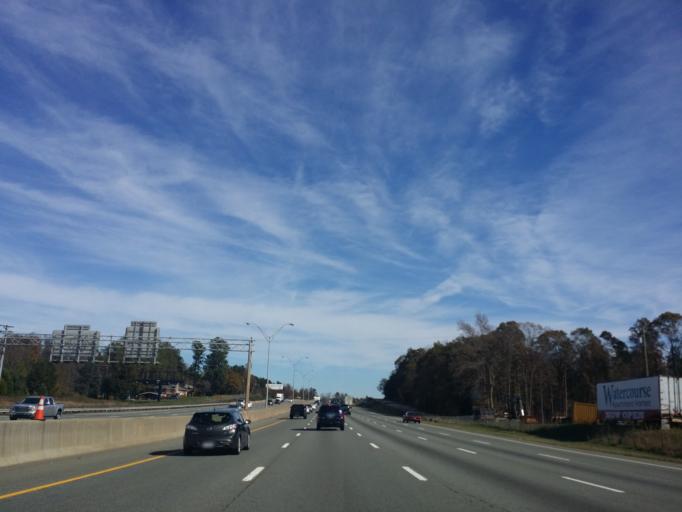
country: US
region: North Carolina
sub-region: Alamance County
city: Graham
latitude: 36.0646
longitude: -79.3815
